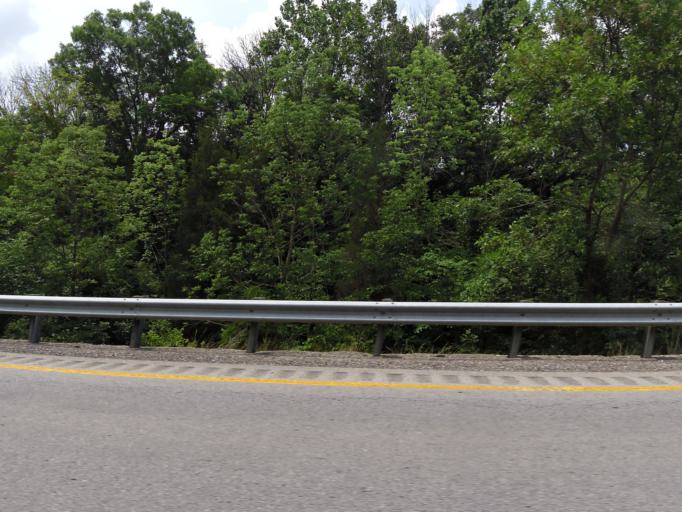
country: US
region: Kentucky
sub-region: Oldham County
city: La Grange
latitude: 38.4670
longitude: -85.2822
